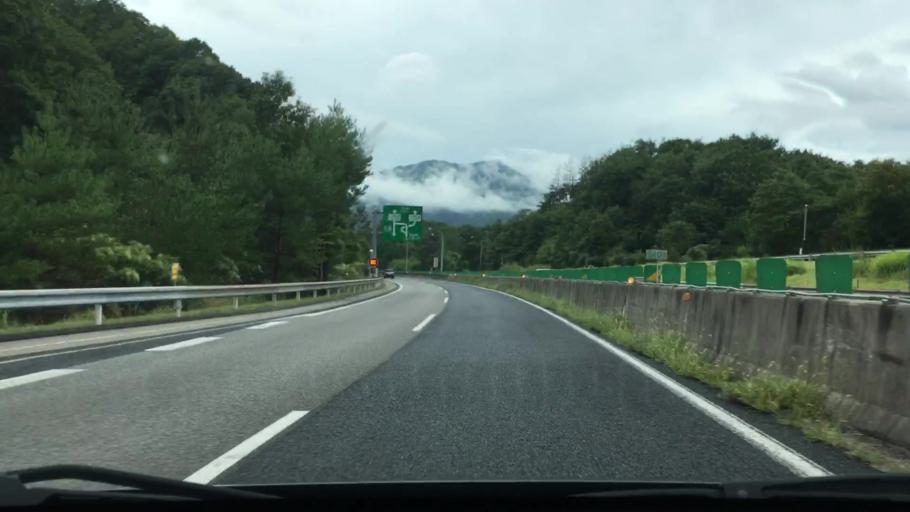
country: JP
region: Hiroshima
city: Hiroshima-shi
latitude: 34.5861
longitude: 132.4772
